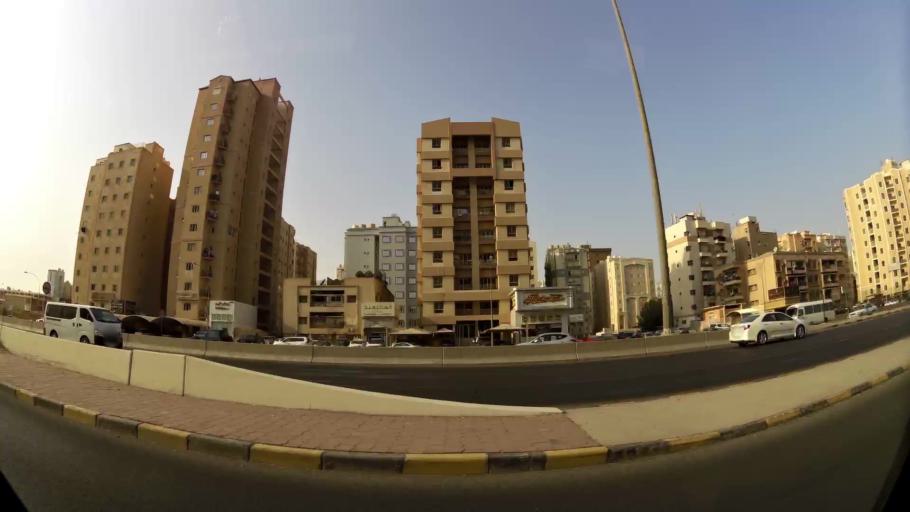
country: KW
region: Muhafazat Hawalli
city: Hawalli
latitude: 29.3236
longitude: 48.0161
